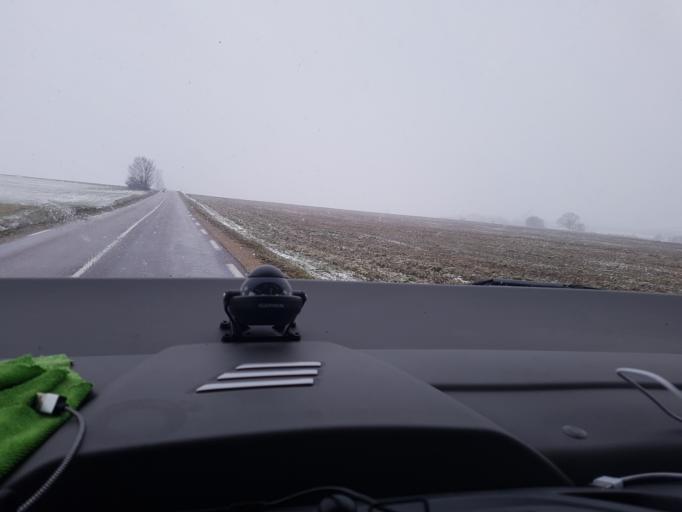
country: FR
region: Lorraine
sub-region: Departement de Meurthe-et-Moselle
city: Baccarat
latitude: 48.5297
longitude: 6.8044
